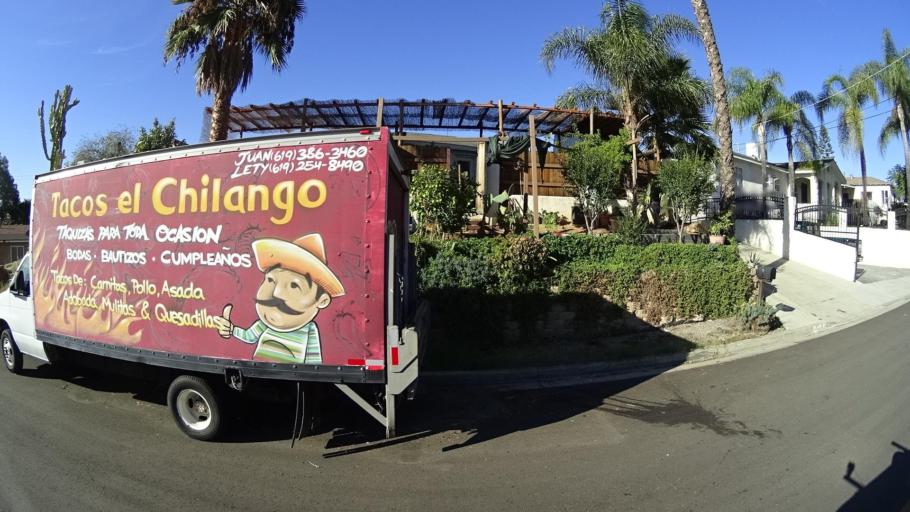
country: US
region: California
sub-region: San Diego County
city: La Presa
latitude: 32.7110
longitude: -116.9900
